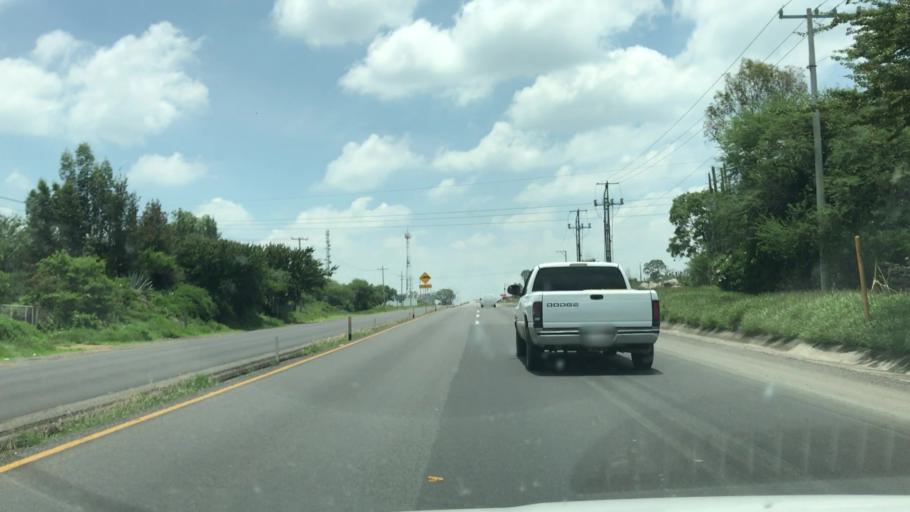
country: MX
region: Guanajuato
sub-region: Irapuato
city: San Ignacio de Rivera (Ojo de Agua)
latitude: 20.5587
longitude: -101.4498
